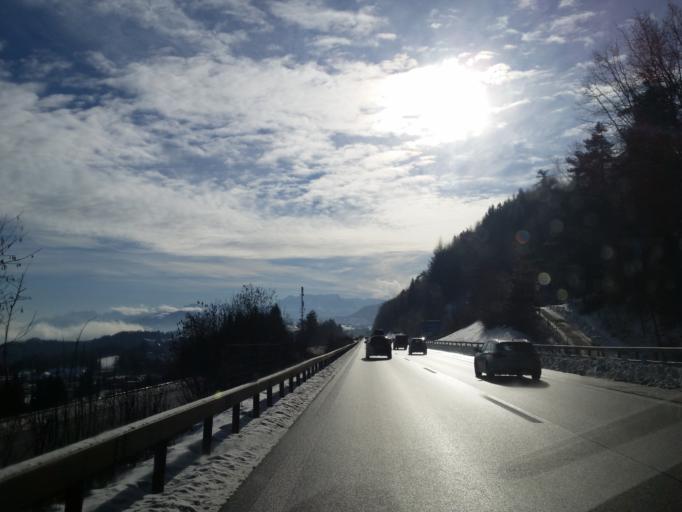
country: CH
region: Zurich
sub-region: Bezirk Horgen
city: Horgen / Oberdorf
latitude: 47.2500
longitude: 8.5950
